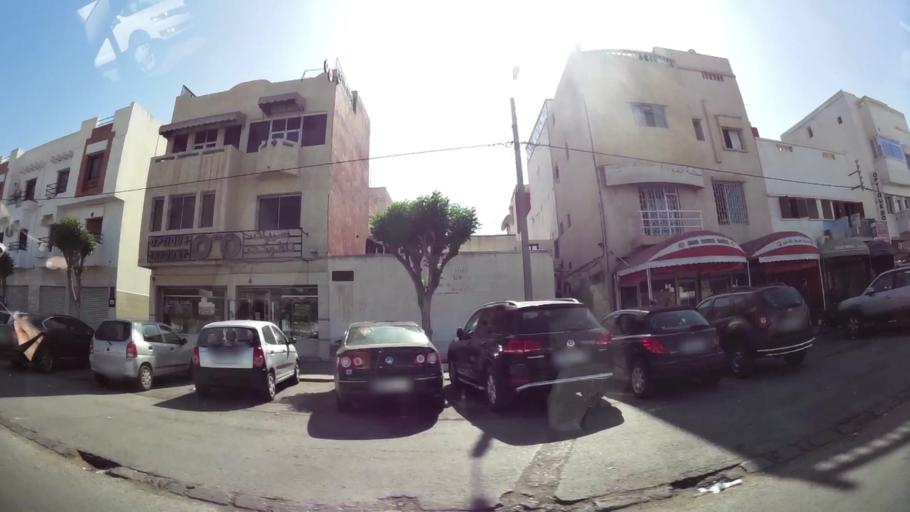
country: MA
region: Souss-Massa-Draa
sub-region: Agadir-Ida-ou-Tnan
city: Agadir
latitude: 30.4144
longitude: -9.5887
